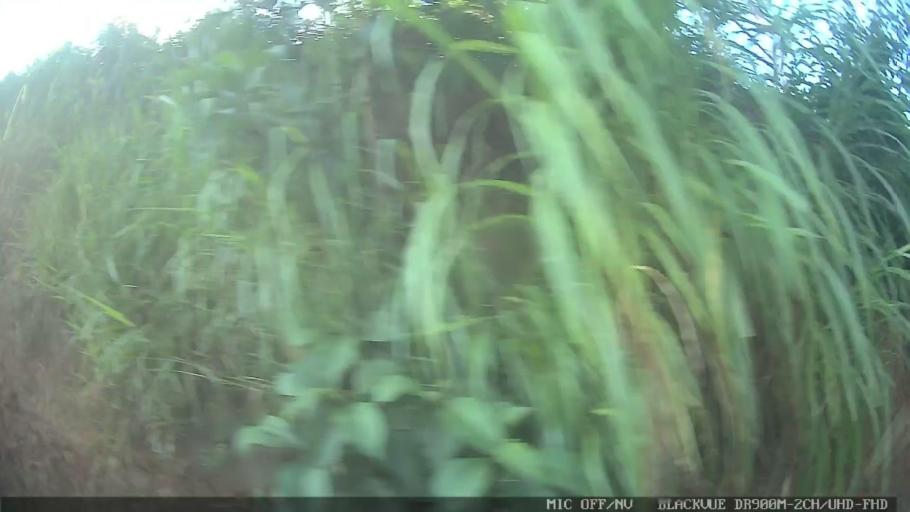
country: BR
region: Sao Paulo
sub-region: Braganca Paulista
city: Braganca Paulista
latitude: -22.9164
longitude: -46.4385
